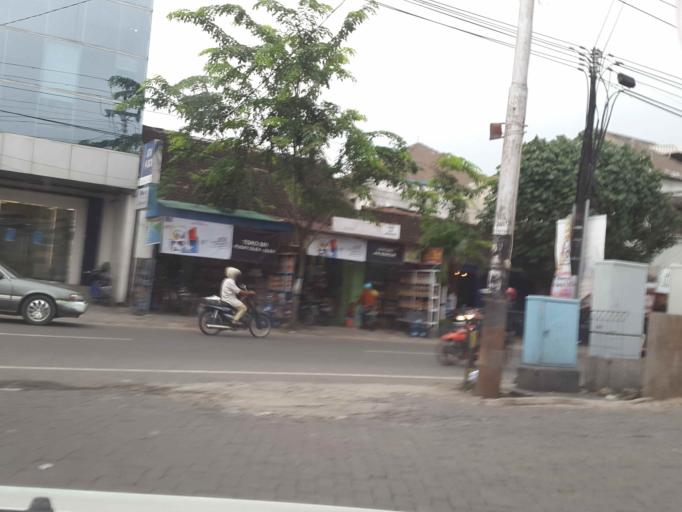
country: ID
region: Central Java
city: Surakarta
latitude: -7.5477
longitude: 110.8211
